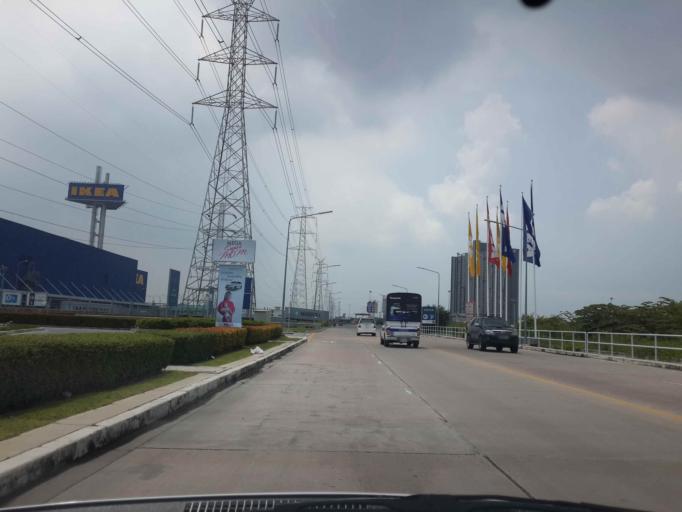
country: TH
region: Bangkok
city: Bang Na
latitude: 13.6448
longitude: 100.6773
